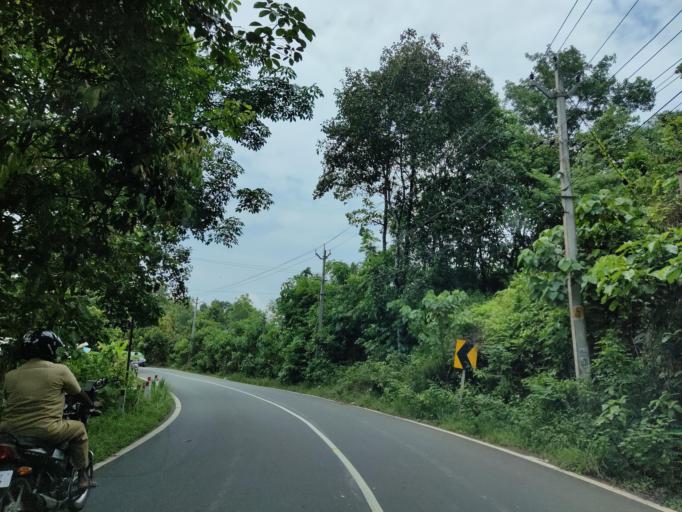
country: IN
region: Kerala
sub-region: Alappuzha
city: Chengannur
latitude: 9.2766
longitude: 76.6155
